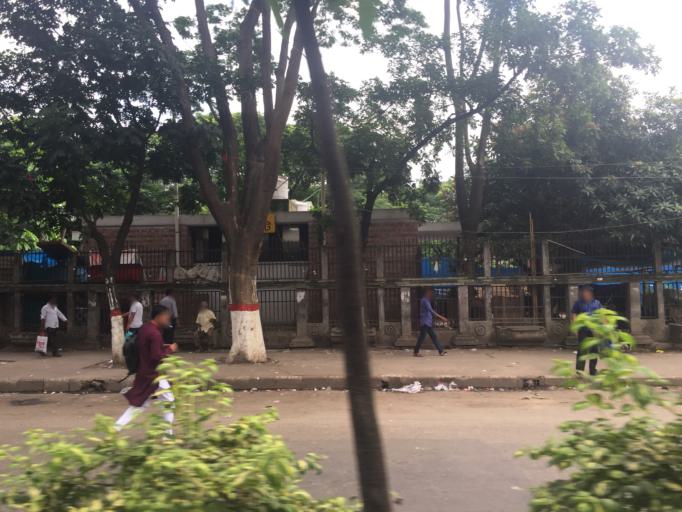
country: BD
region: Dhaka
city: Paltan
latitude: 23.7249
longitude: 90.4100
